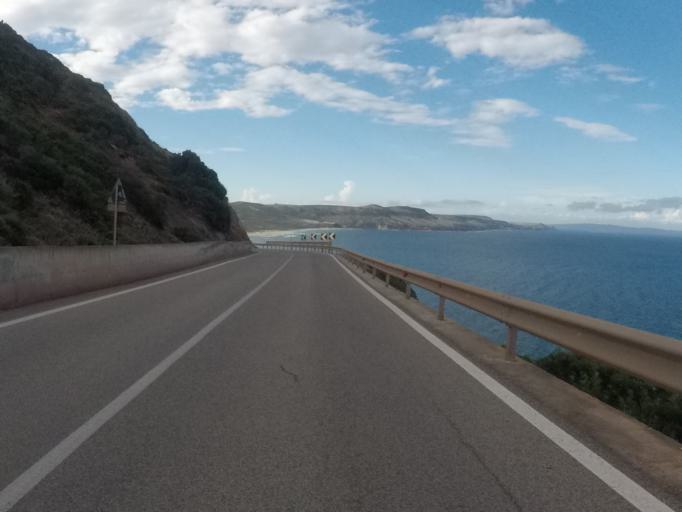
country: IT
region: Sardinia
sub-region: Provincia di Carbonia-Iglesias
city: Gonnesa
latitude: 39.3012
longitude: 8.4359
